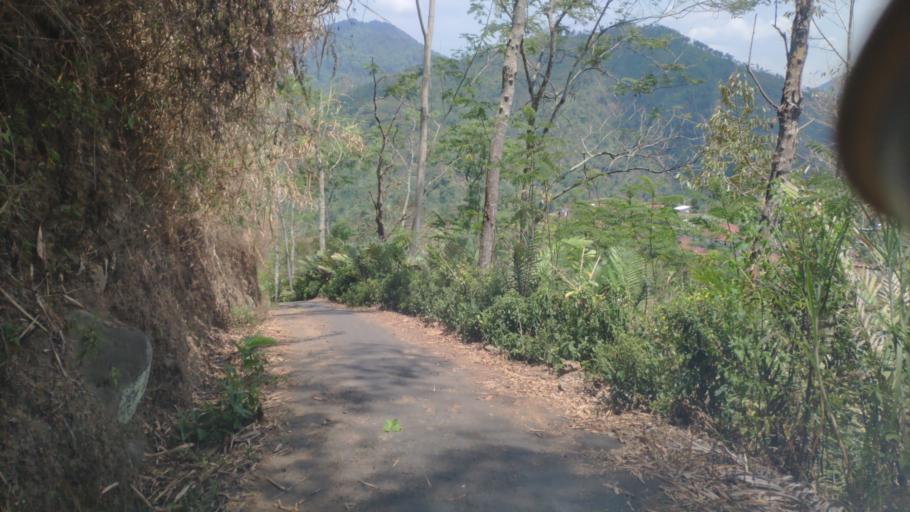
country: ID
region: Central Java
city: Wonosobo
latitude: -7.3395
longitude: 109.7243
